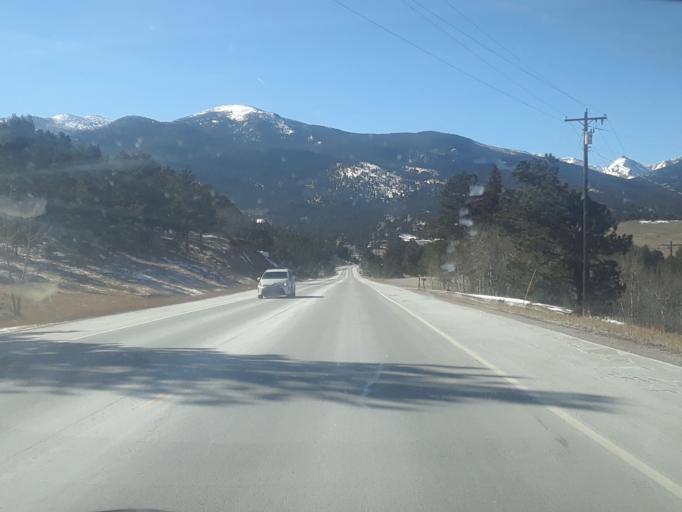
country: US
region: Colorado
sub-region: Larimer County
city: Estes Park
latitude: 40.1888
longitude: -105.4972
